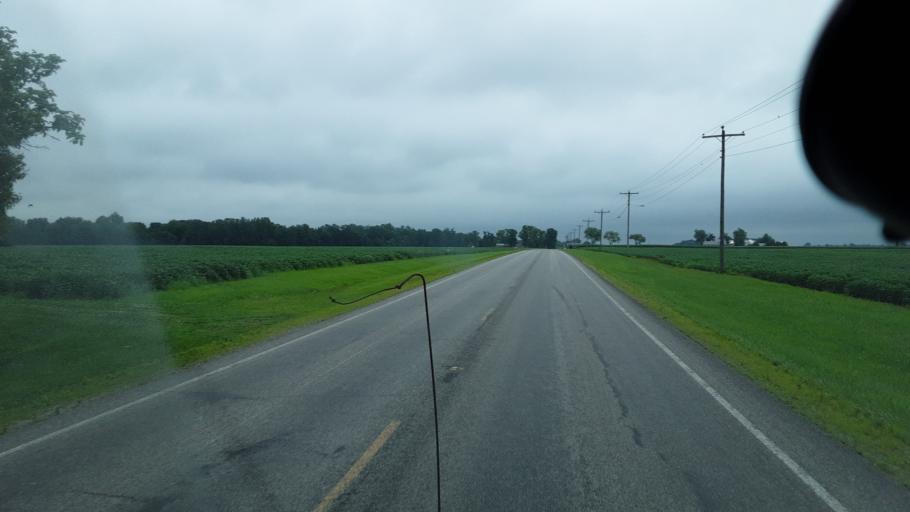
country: US
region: Indiana
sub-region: Wells County
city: Bluffton
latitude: 40.6940
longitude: -85.0828
